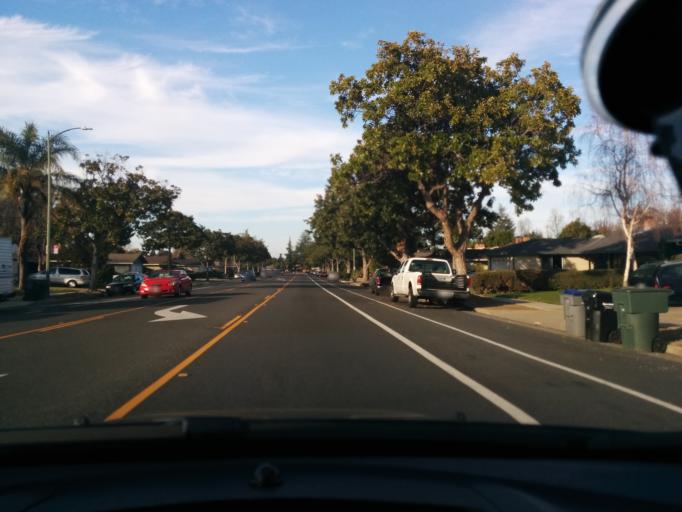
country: US
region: California
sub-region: Santa Clara County
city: Sunnyvale
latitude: 37.3453
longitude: -122.0500
